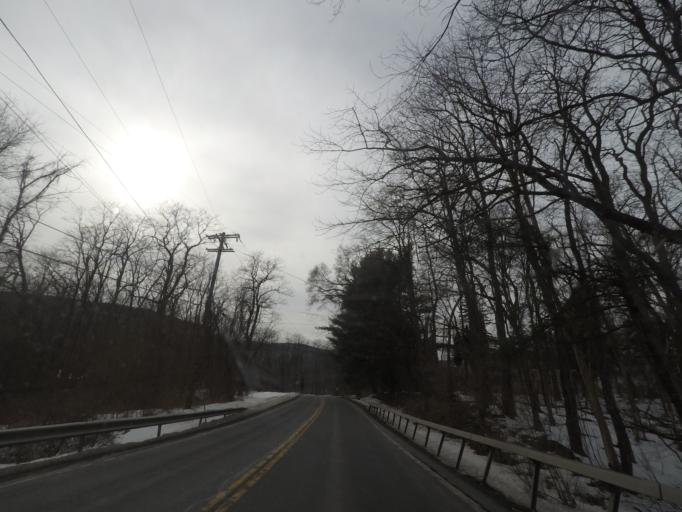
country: US
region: New York
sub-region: Albany County
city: Voorheesville
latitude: 42.6584
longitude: -73.9885
